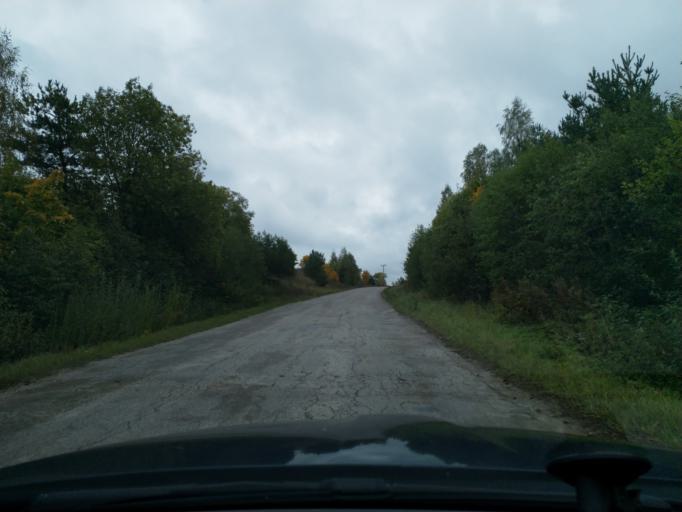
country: LV
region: Alsunga
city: Alsunga
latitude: 57.0242
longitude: 21.6834
